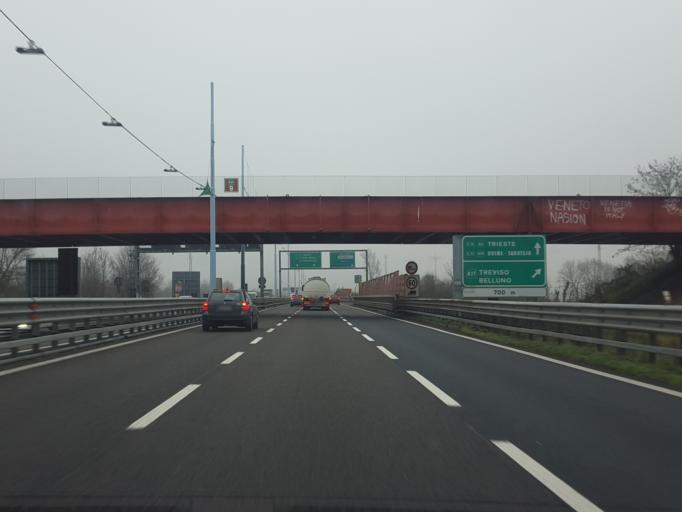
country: IT
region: Veneto
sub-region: Provincia di Treviso
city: Mogliano Veneto
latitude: 45.5284
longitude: 12.2660
